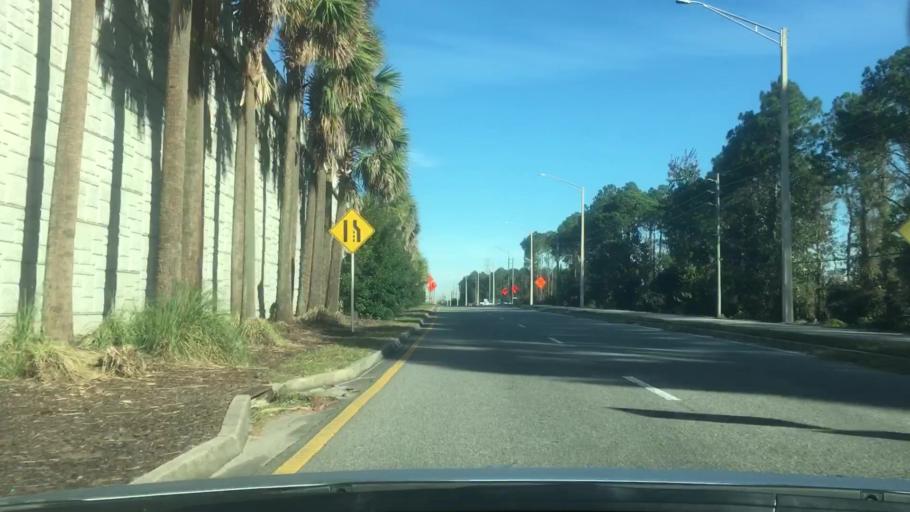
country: US
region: Florida
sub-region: Duval County
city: Neptune Beach
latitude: 30.2881
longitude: -81.4887
